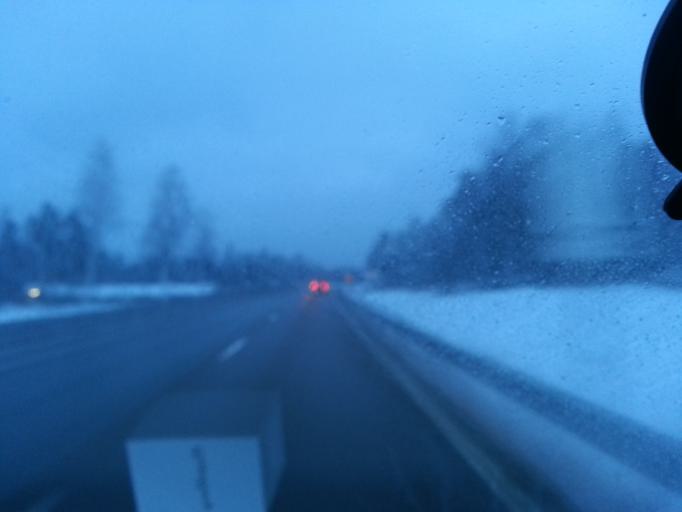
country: SE
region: Kronoberg
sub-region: Ljungby Kommun
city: Lagan
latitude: 56.9220
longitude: 13.9747
